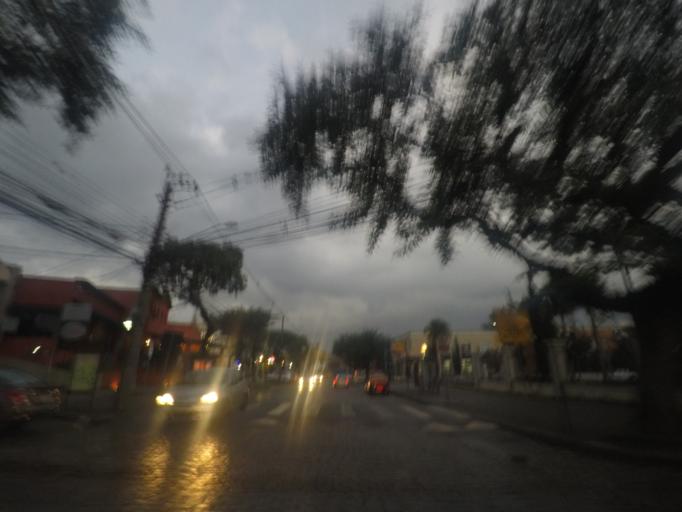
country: BR
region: Parana
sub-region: Curitiba
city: Curitiba
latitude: -25.4045
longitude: -49.3279
